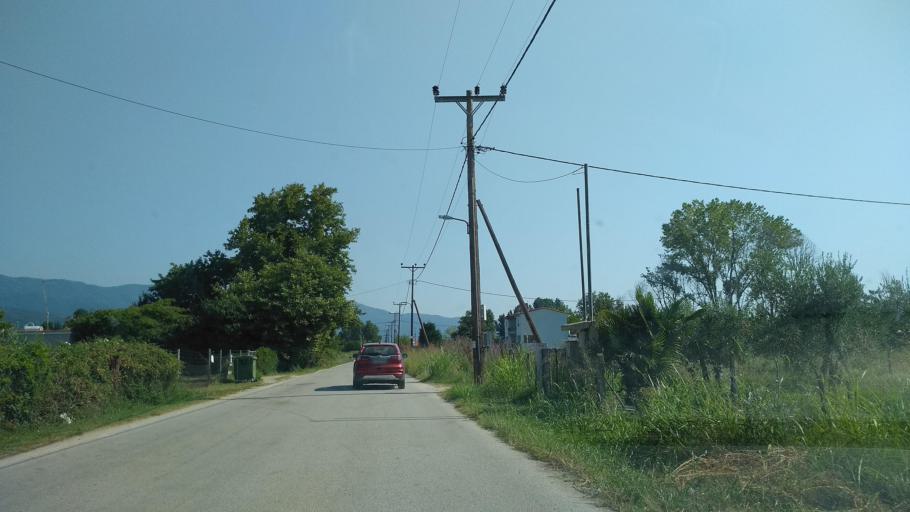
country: GR
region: Central Macedonia
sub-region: Nomos Thessalonikis
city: Stavros
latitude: 40.6817
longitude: 23.6873
